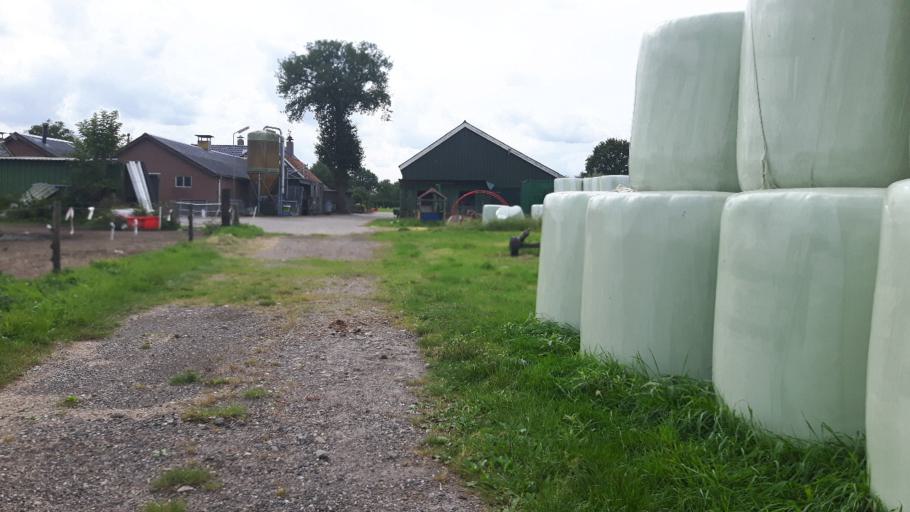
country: NL
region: Gelderland
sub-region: Gemeente Putten
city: Putten
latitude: 52.2592
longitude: 5.5503
